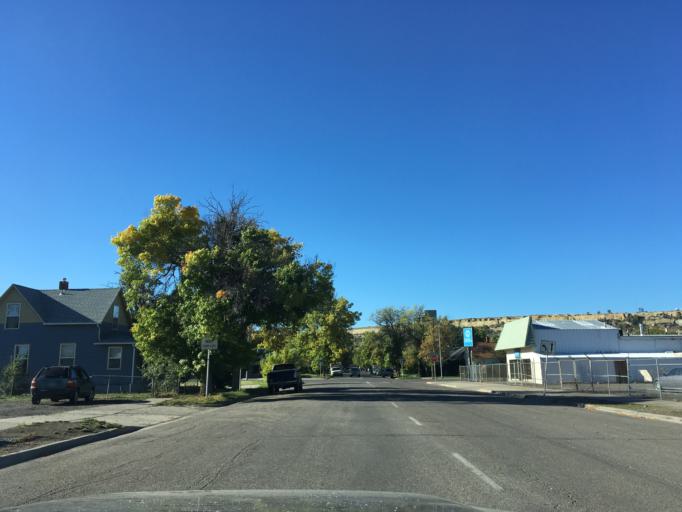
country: US
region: Montana
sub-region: Yellowstone County
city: Billings
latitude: 45.7875
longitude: -108.5057
